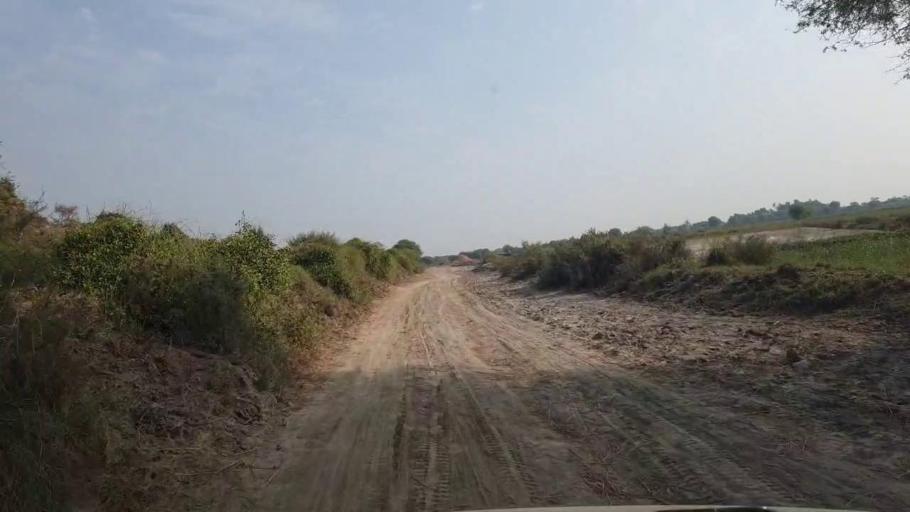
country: PK
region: Sindh
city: Talhar
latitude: 24.9030
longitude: 68.8953
